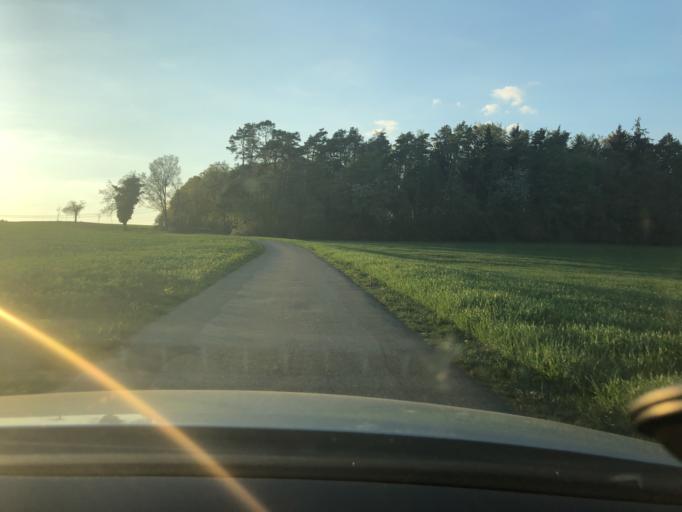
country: DE
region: Baden-Wuerttemberg
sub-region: Freiburg Region
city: Waldshut-Tiengen
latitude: 47.6491
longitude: 8.1886
